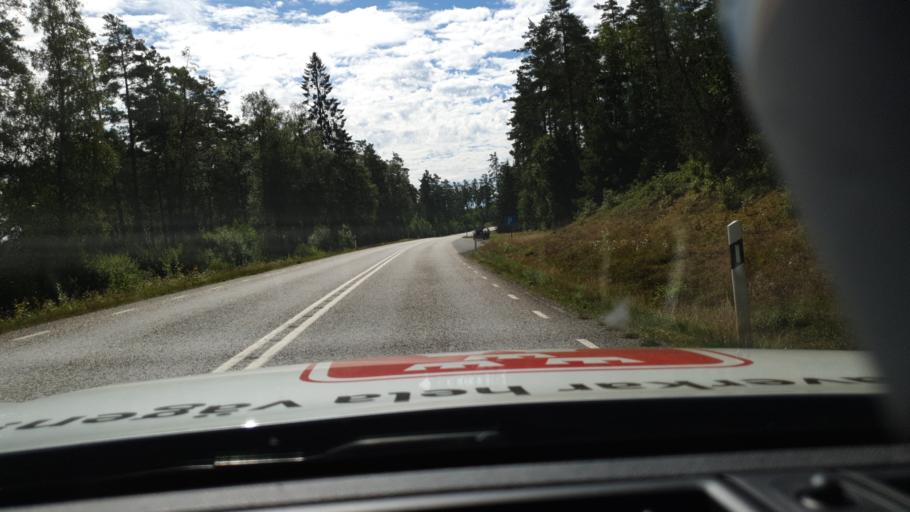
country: SE
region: Joenkoeping
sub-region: Jonkopings Kommun
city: Odensjo
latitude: 57.6049
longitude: 14.2184
